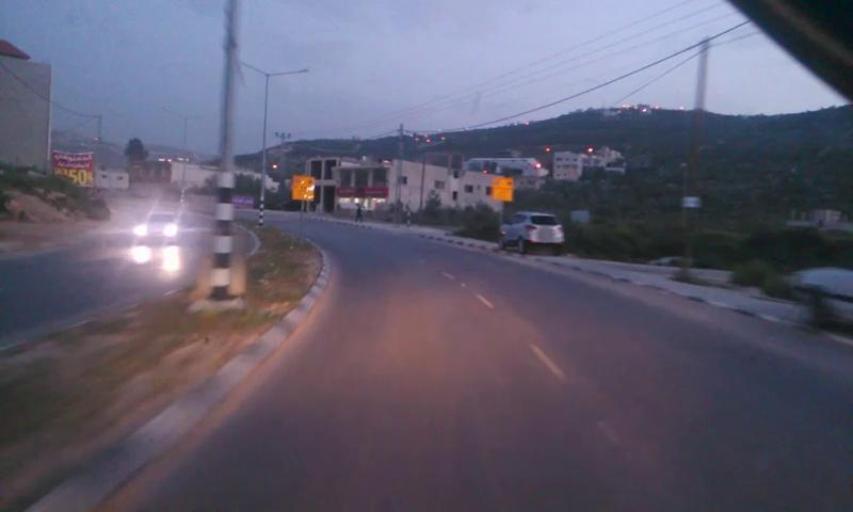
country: PS
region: West Bank
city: Dayr Sharaf
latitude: 32.2523
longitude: 35.1863
